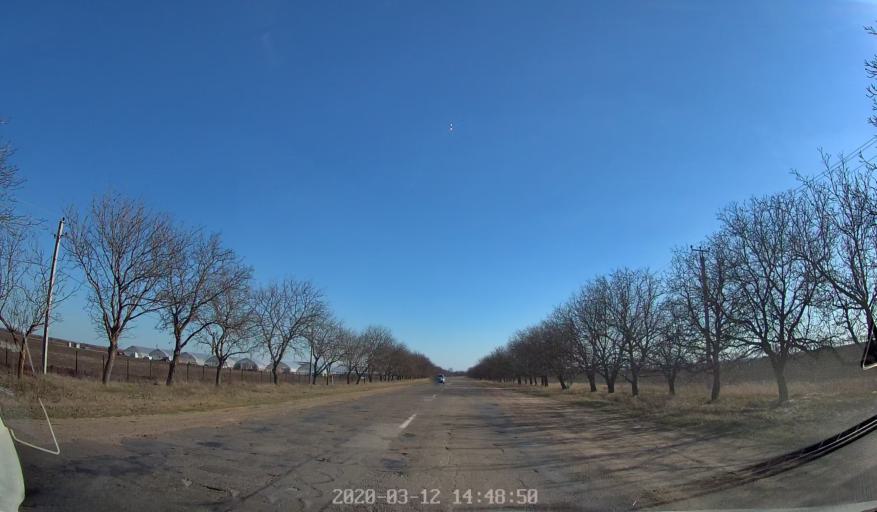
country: MD
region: Criuleni
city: Criuleni
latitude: 47.2291
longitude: 29.1416
